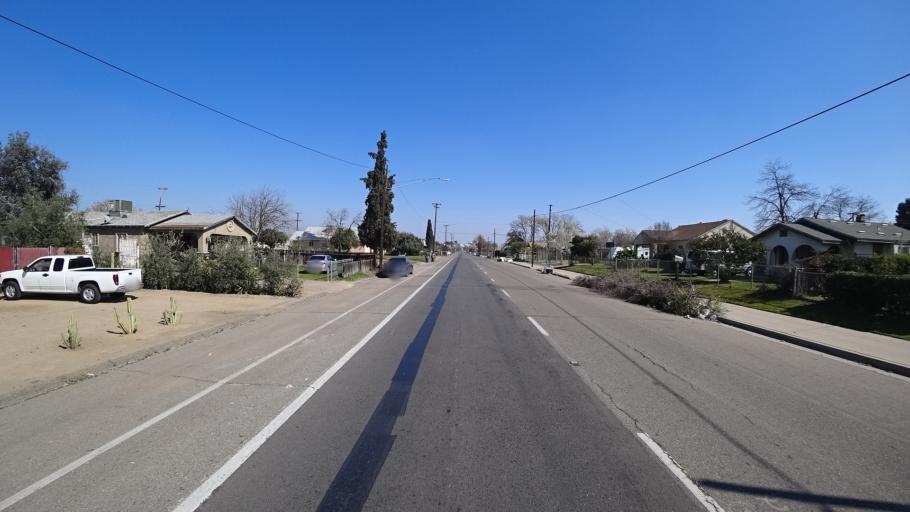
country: US
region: California
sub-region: Fresno County
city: West Park
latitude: 36.7358
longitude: -119.8162
